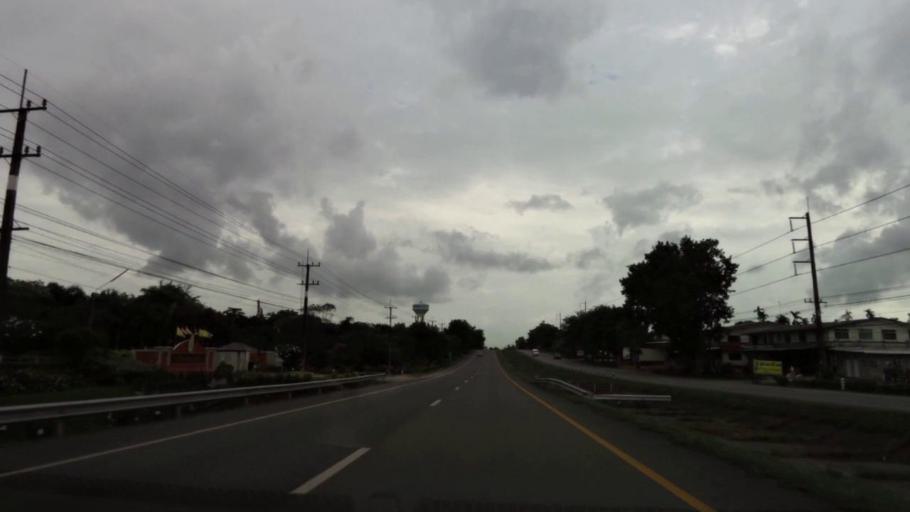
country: TH
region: Chanthaburi
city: Tha Mai
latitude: 12.7017
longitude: 101.9856
